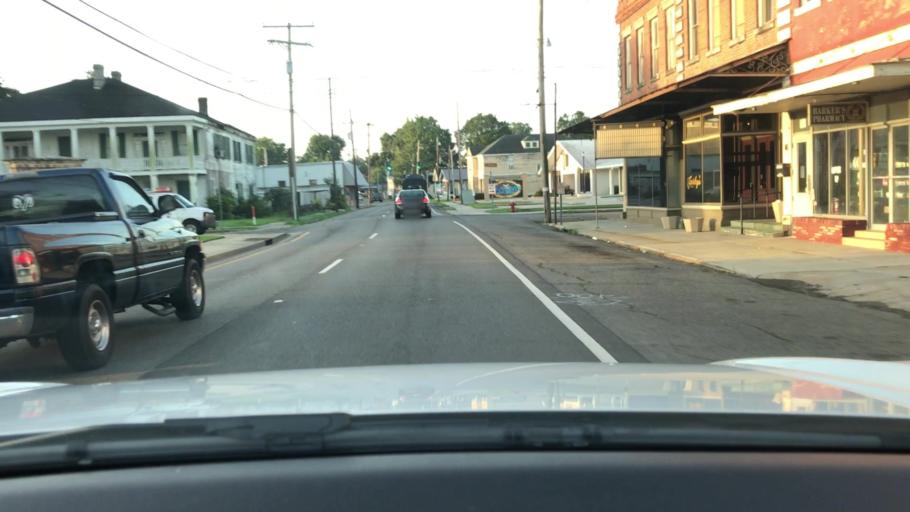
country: US
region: Louisiana
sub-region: Iberville Parish
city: Plaquemine
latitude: 30.2904
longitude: -91.2352
